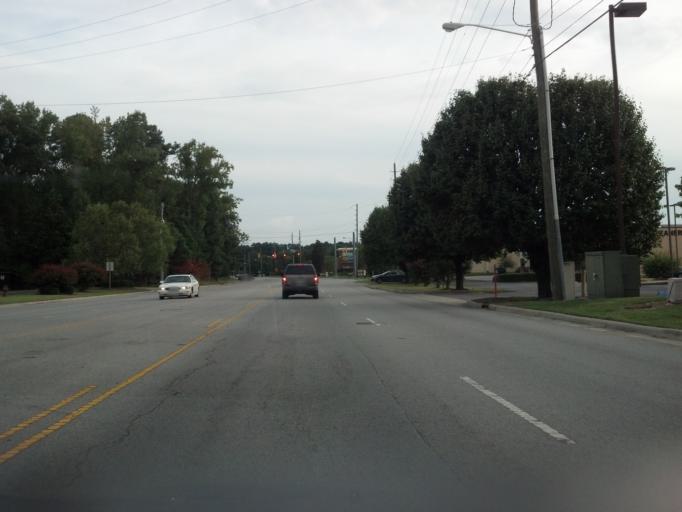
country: US
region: North Carolina
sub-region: Pitt County
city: Summerfield
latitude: 35.5760
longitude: -77.3821
